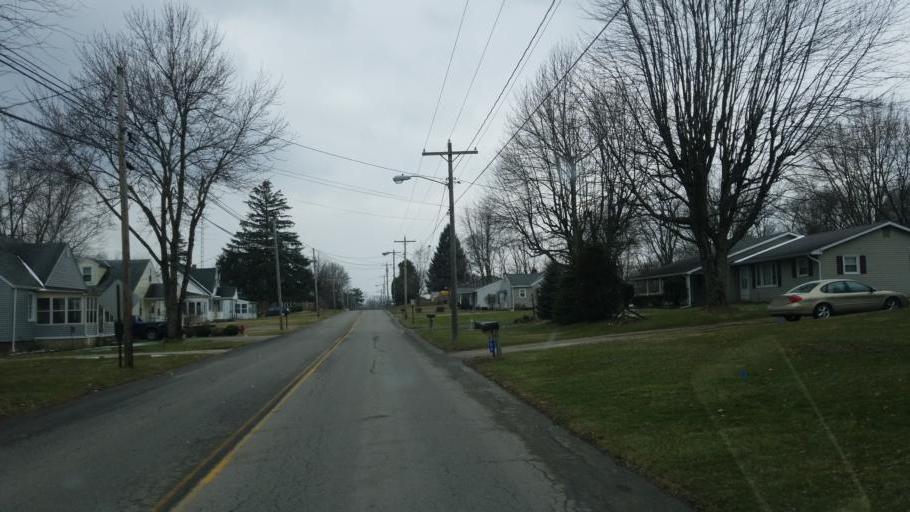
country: US
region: Ohio
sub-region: Crawford County
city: Galion
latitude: 40.7376
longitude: -82.7712
